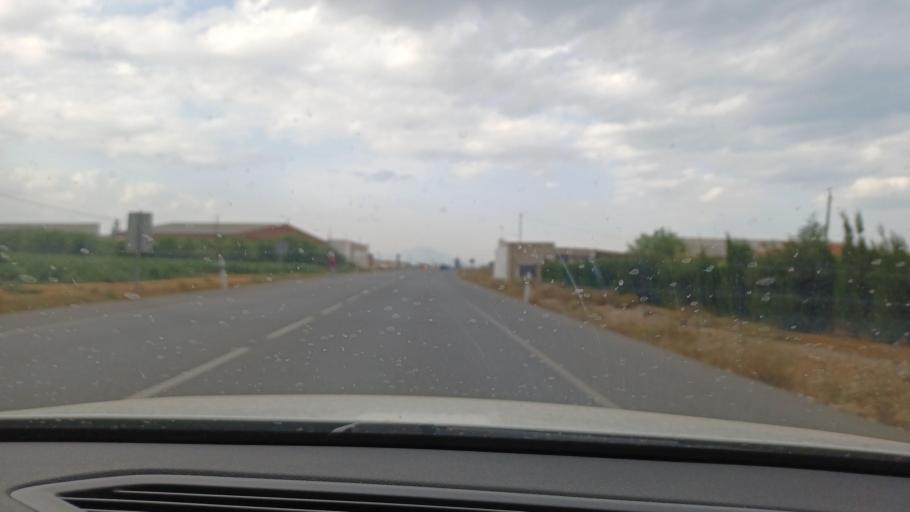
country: ES
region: Valencia
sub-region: Provincia de Castello
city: Benicarlo
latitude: 40.4365
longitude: 0.4398
